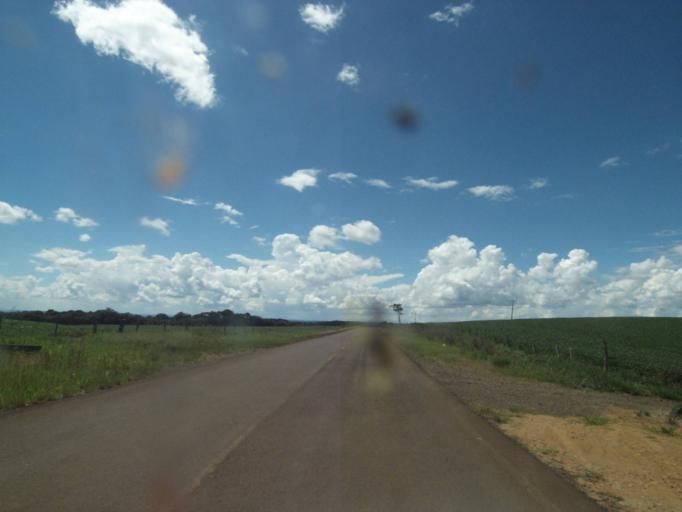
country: BR
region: Parana
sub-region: Pinhao
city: Pinhao
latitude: -25.8026
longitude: -52.0737
